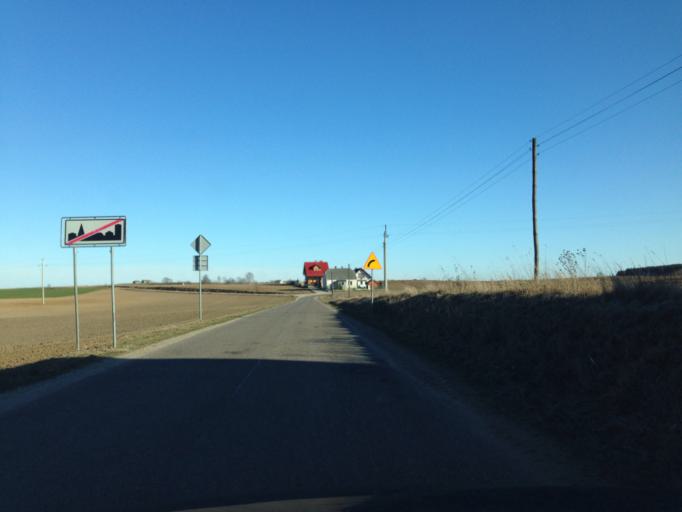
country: PL
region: Kujawsko-Pomorskie
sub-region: Powiat brodnicki
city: Brzozie
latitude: 53.3327
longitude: 19.6570
